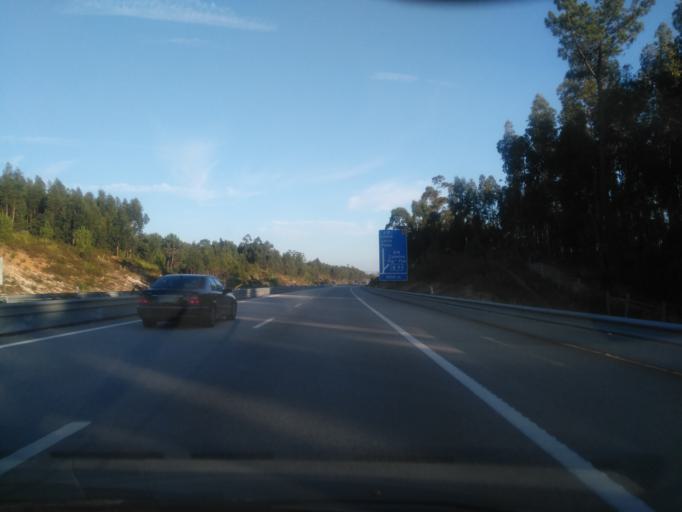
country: PT
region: Coimbra
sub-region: Figueira da Foz
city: Alhadas
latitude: 40.1695
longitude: -8.7881
